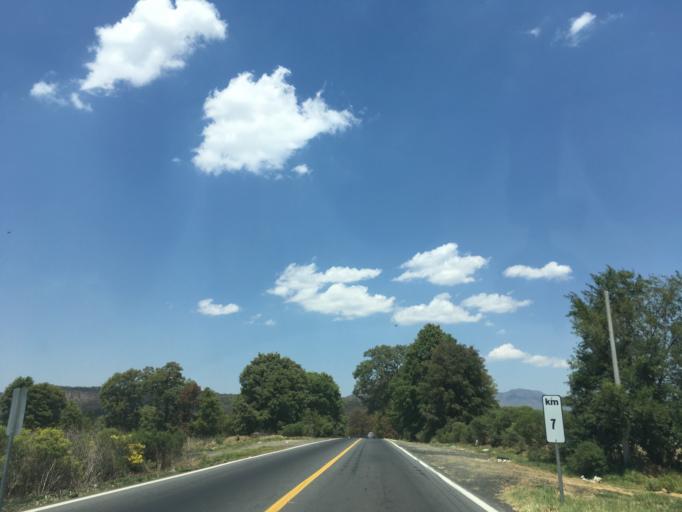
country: MX
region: Mexico
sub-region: Chalco
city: Zopoco
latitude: 19.7948
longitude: -102.0260
